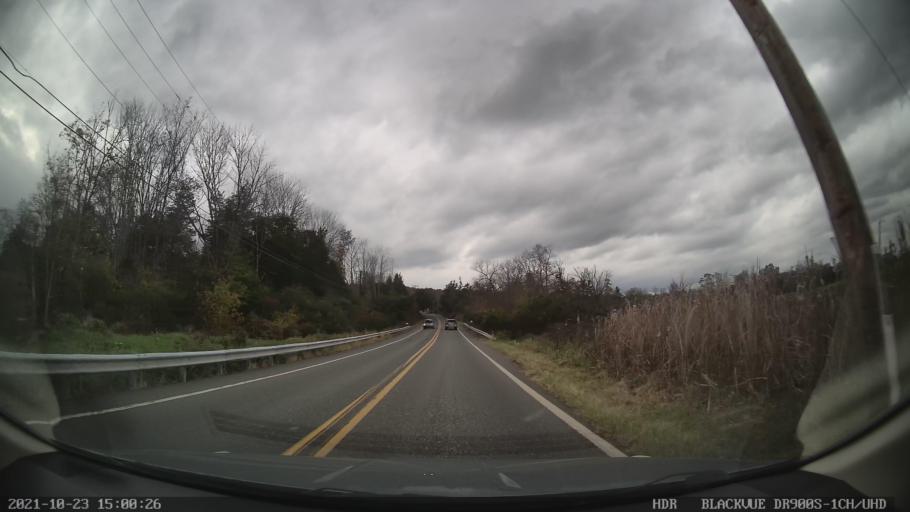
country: US
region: Pennsylvania
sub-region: Montgomery County
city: East Greenville
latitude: 40.3981
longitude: -75.5378
